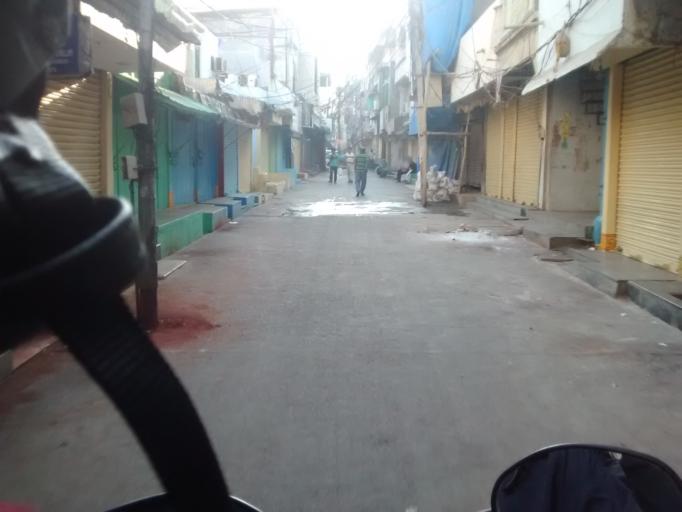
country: IN
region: Telangana
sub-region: Hyderabad
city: Malkajgiri
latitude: 17.4377
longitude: 78.4907
